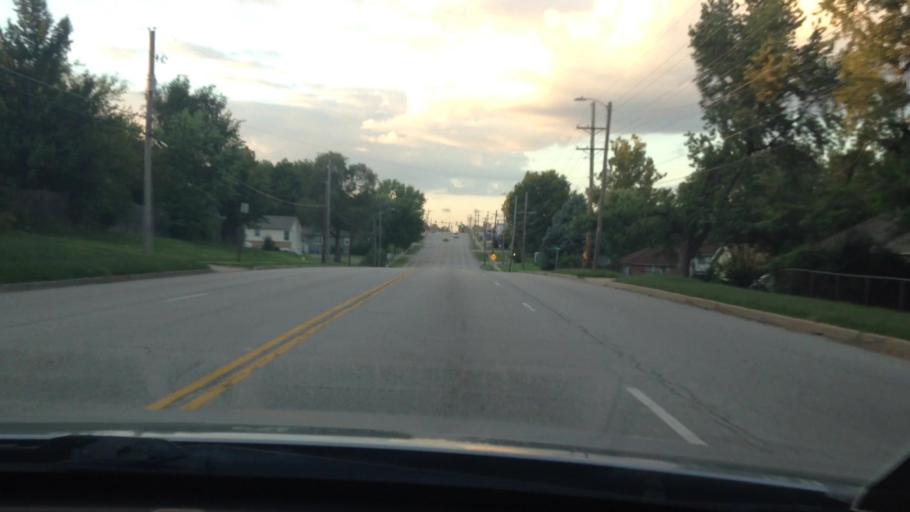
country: US
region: Missouri
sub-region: Jackson County
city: Raytown
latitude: 38.9816
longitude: -94.4646
